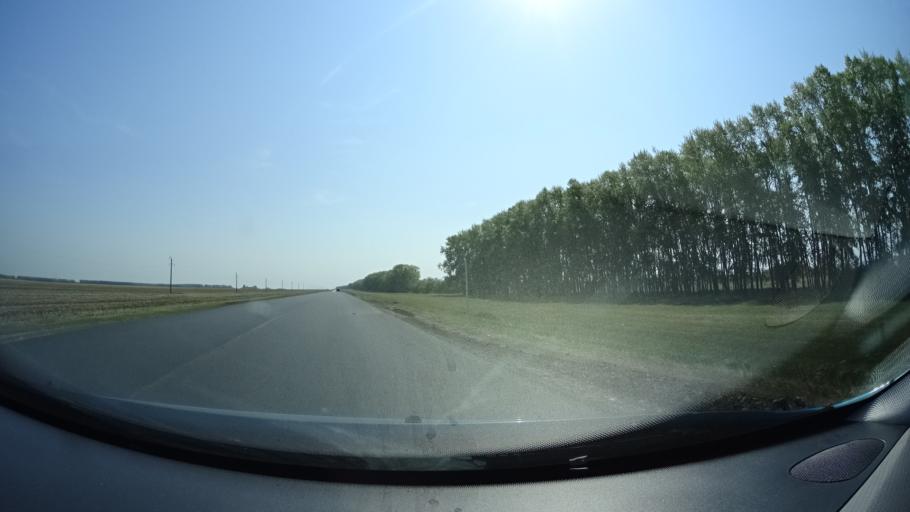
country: RU
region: Bashkortostan
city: Karmaskaly
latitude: 54.4173
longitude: 56.0517
